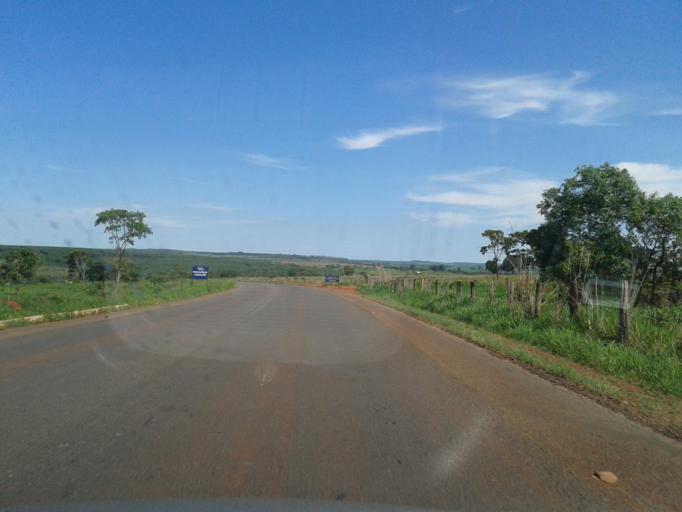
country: BR
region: Goias
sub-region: Bela Vista De Goias
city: Bela Vista de Goias
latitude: -17.1806
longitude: -48.7167
